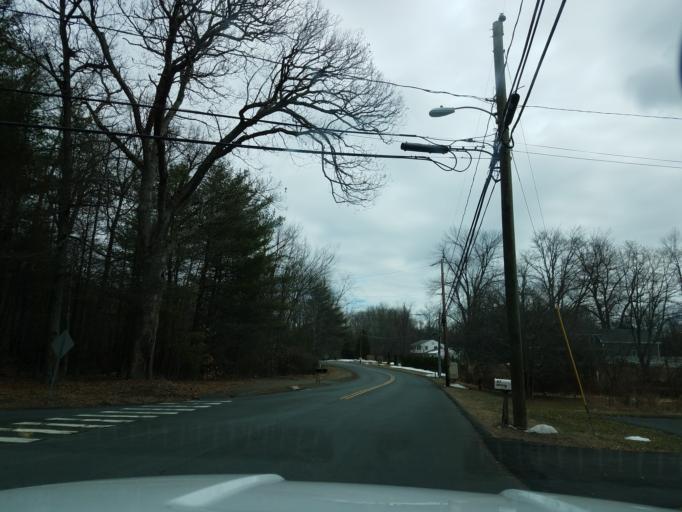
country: US
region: Connecticut
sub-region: Hartford County
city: Farmington
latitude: 41.7778
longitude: -72.8495
